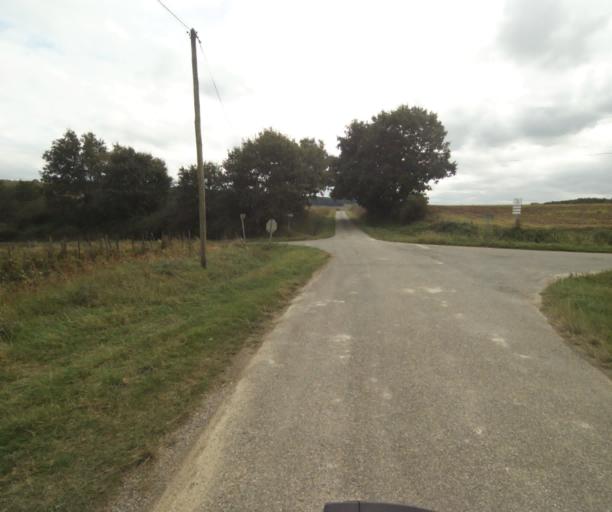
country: FR
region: Midi-Pyrenees
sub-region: Departement du Tarn-et-Garonne
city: Beaumont-de-Lomagne
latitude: 43.8229
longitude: 1.0844
